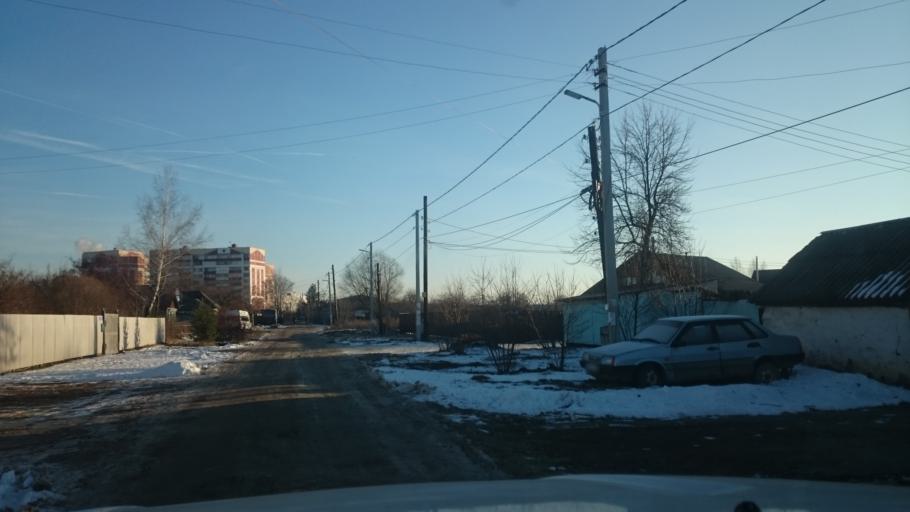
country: RU
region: Tula
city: Tula
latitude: 54.2017
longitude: 37.6926
